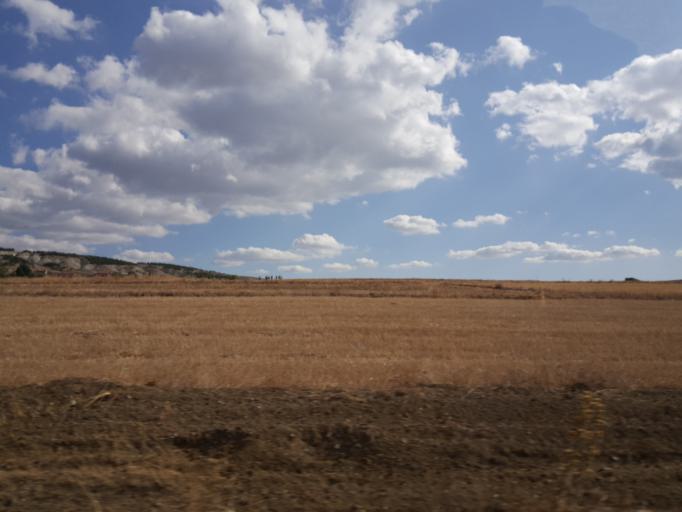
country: TR
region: Tokat
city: Sulusaray
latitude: 39.9880
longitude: 35.9843
